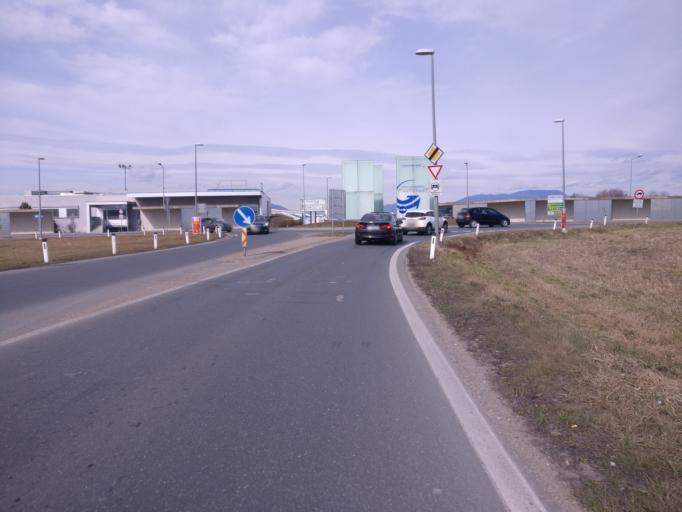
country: AT
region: Styria
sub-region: Politischer Bezirk Graz-Umgebung
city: Feldkirchen bei Graz
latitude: 46.9961
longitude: 15.4471
